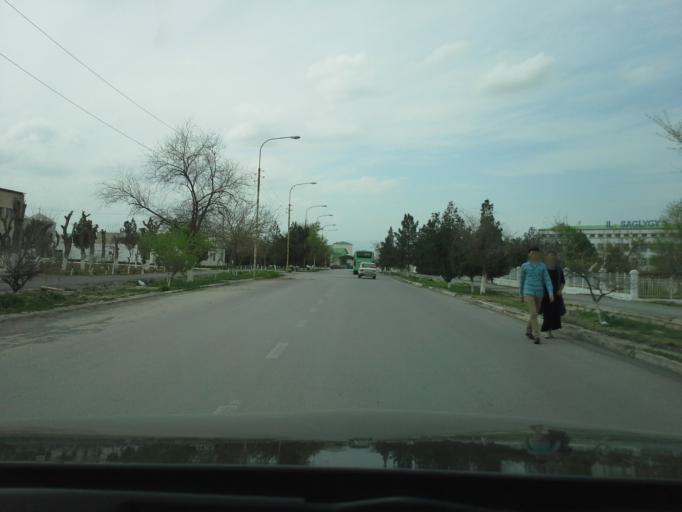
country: TM
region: Ahal
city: Abadan
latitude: 38.0590
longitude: 58.1456
